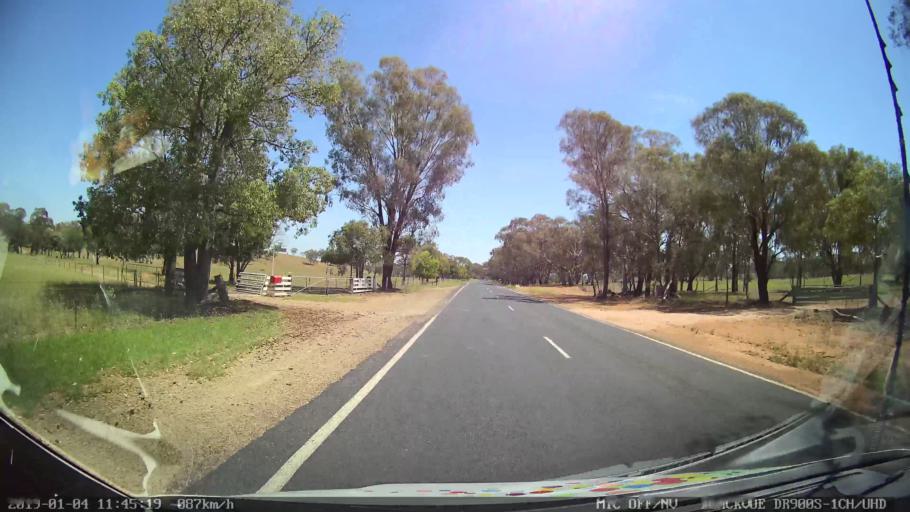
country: AU
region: New South Wales
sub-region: Cabonne
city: Molong
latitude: -32.9553
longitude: 148.7639
